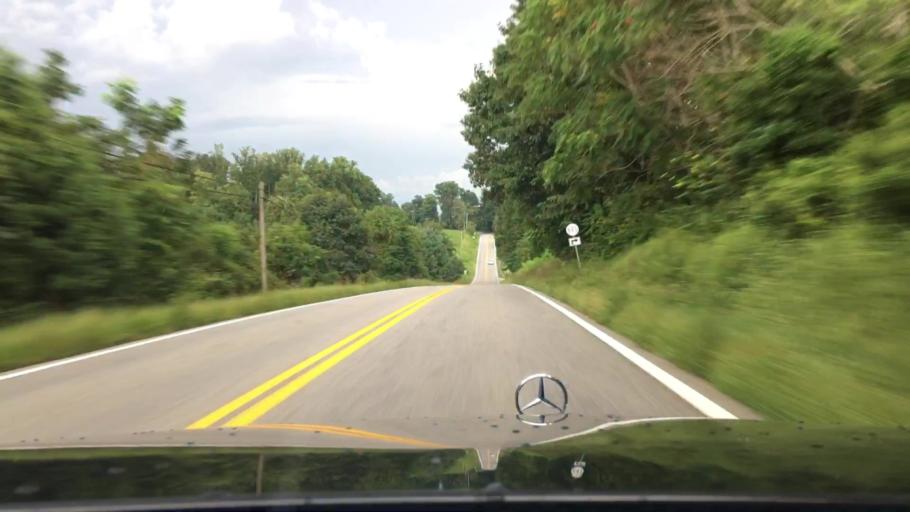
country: US
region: Virginia
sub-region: Nelson County
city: Lovingston
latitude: 37.7808
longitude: -78.9793
